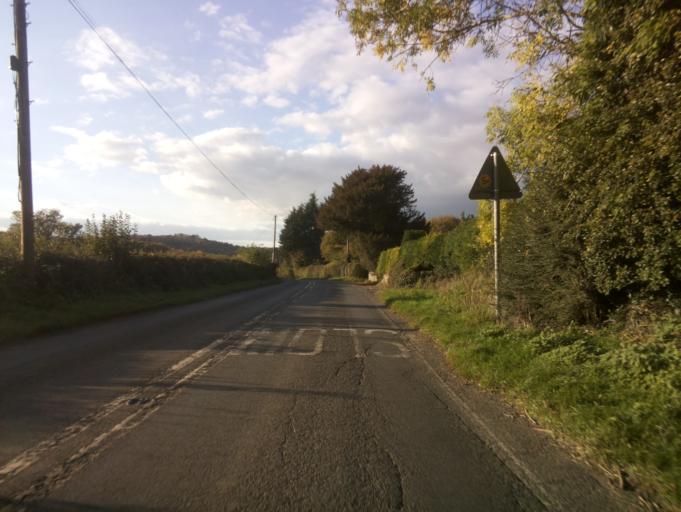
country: GB
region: England
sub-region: Herefordshire
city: Donnington
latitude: 52.0294
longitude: -2.3769
